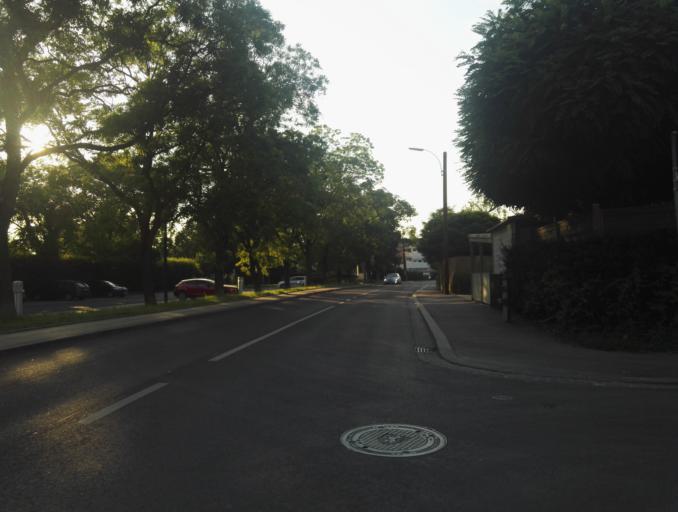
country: AT
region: Styria
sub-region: Graz Stadt
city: Graz
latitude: 47.0547
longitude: 15.4674
